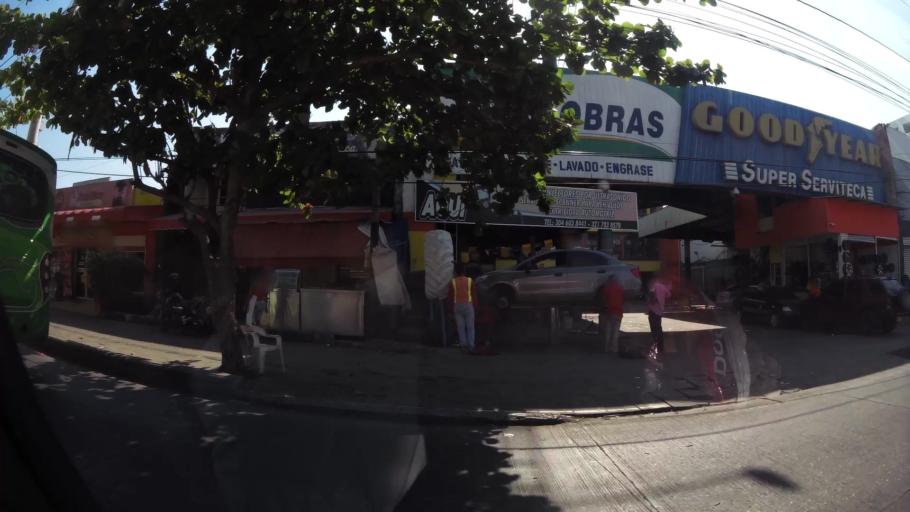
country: CO
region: Bolivar
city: Cartagena
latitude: 10.4037
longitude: -75.4976
